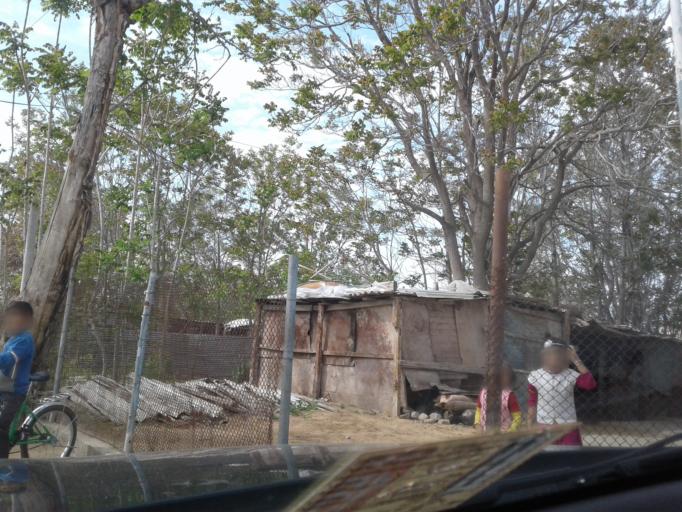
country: TM
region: Ahal
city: Ashgabat
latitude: 37.9783
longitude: 58.2947
